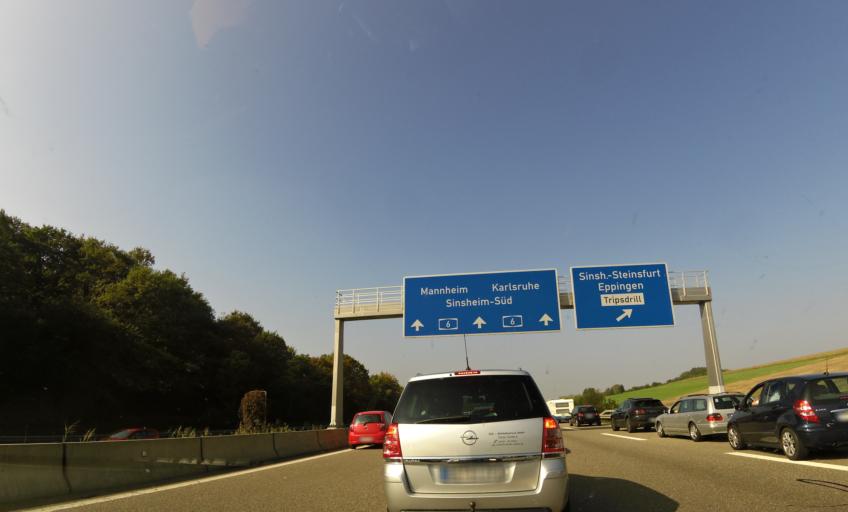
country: DE
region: Baden-Wuerttemberg
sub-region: Regierungsbezirk Stuttgart
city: Ittlingen
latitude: 49.2267
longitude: 8.9262
